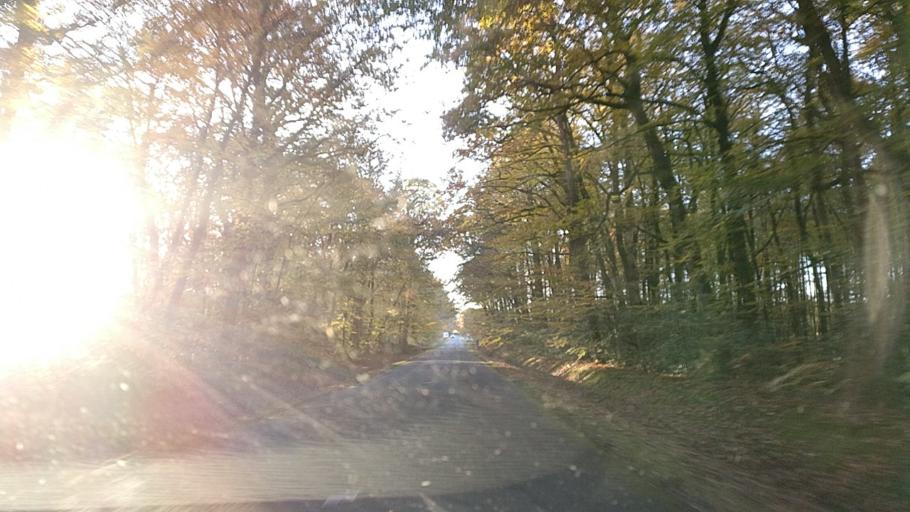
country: FR
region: Brittany
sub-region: Departement d'Ille-et-Vilaine
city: Liffre
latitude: 48.1894
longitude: -1.5351
